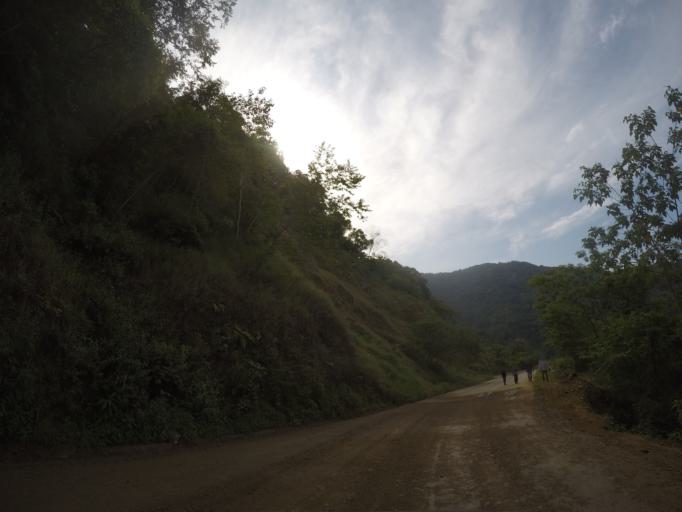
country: MX
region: Oaxaca
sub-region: San Pedro Pochutla
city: Los Naranjos Esquipulas
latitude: 15.9504
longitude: -96.4444
